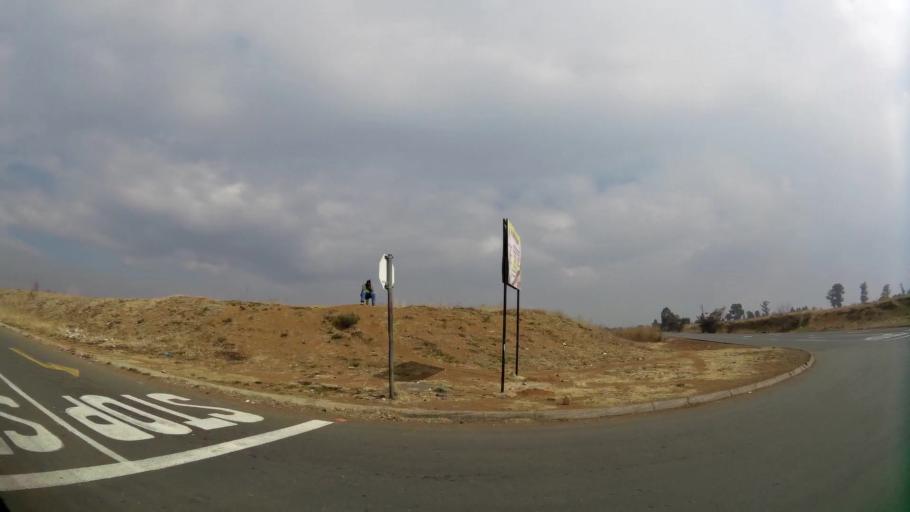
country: ZA
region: Gauteng
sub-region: Sedibeng District Municipality
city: Vanderbijlpark
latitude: -26.6866
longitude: 27.8602
